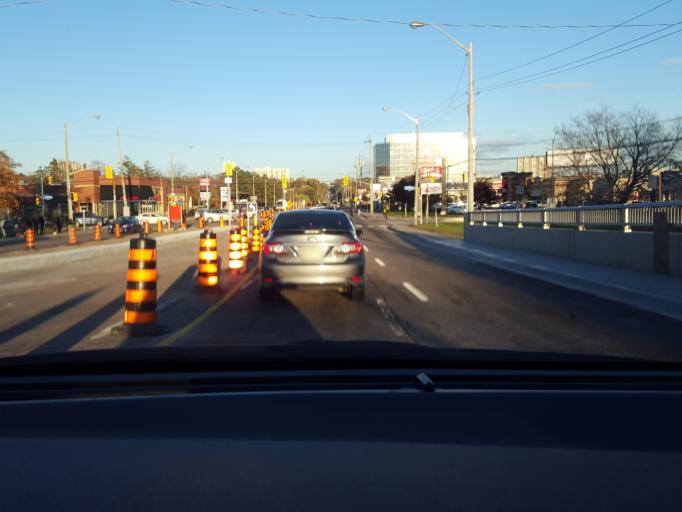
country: CA
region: Ontario
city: Willowdale
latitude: 43.7544
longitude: -79.3530
